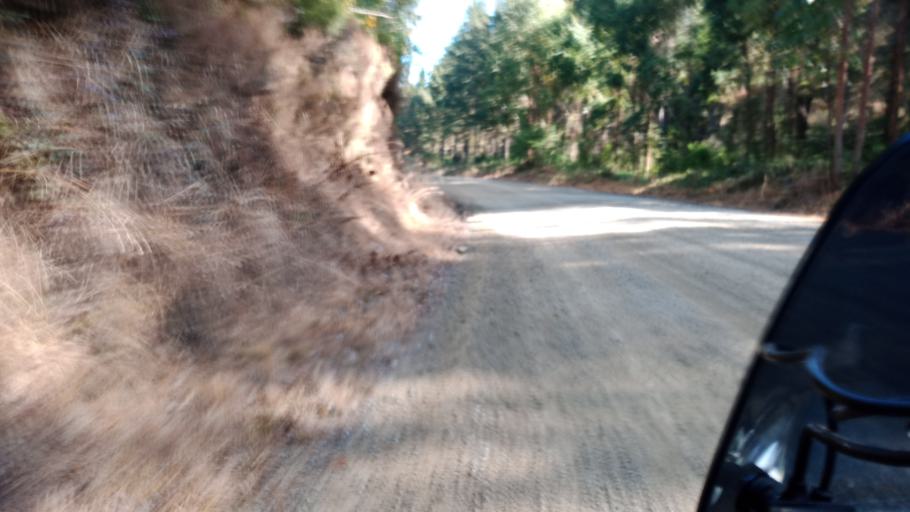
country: NZ
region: Hawke's Bay
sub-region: Wairoa District
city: Wairoa
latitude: -38.9241
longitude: 177.2125
